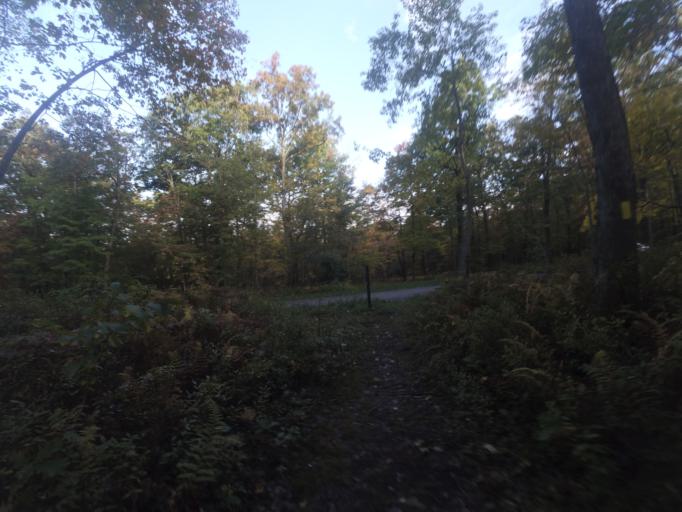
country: US
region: Pennsylvania
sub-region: Centre County
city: Stormstown
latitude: 40.8931
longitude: -78.0016
